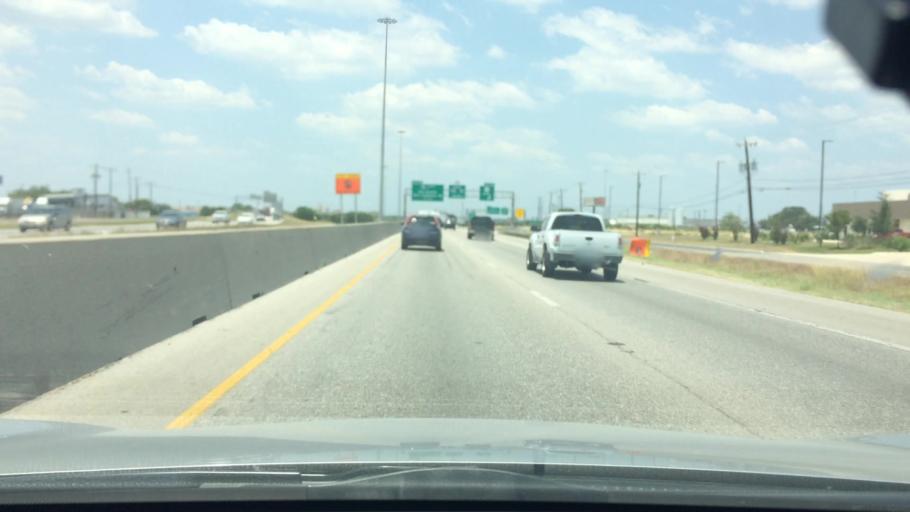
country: US
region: Texas
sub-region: Bexar County
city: Kirby
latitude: 29.4463
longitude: -98.3989
